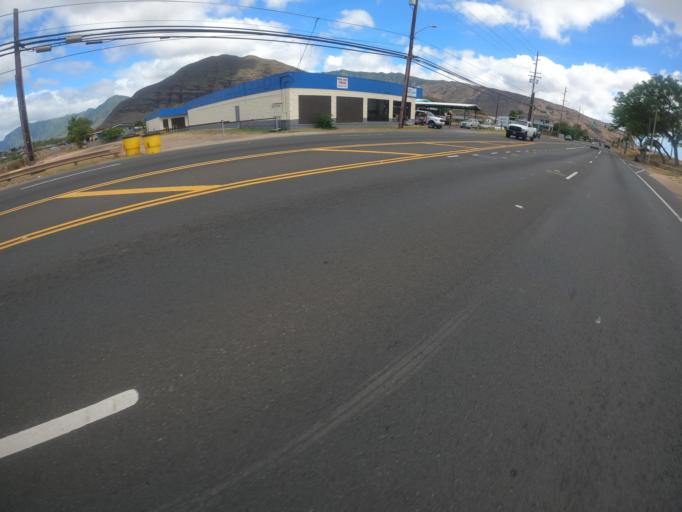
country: US
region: Hawaii
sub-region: Honolulu County
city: Nanakuli
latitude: 21.3921
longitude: -158.1571
